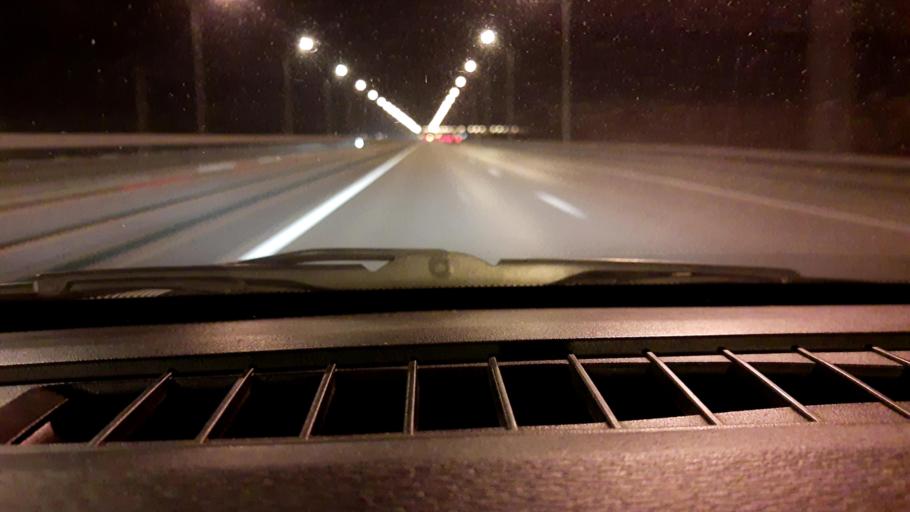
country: RU
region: Nizjnij Novgorod
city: Neklyudovo
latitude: 56.3832
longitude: 43.9628
